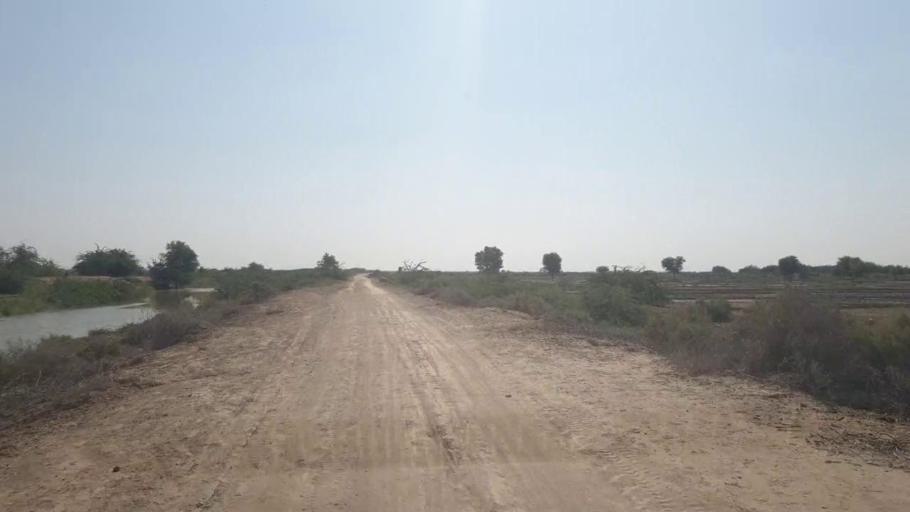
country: PK
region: Sindh
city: Tando Bago
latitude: 24.8801
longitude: 69.1644
